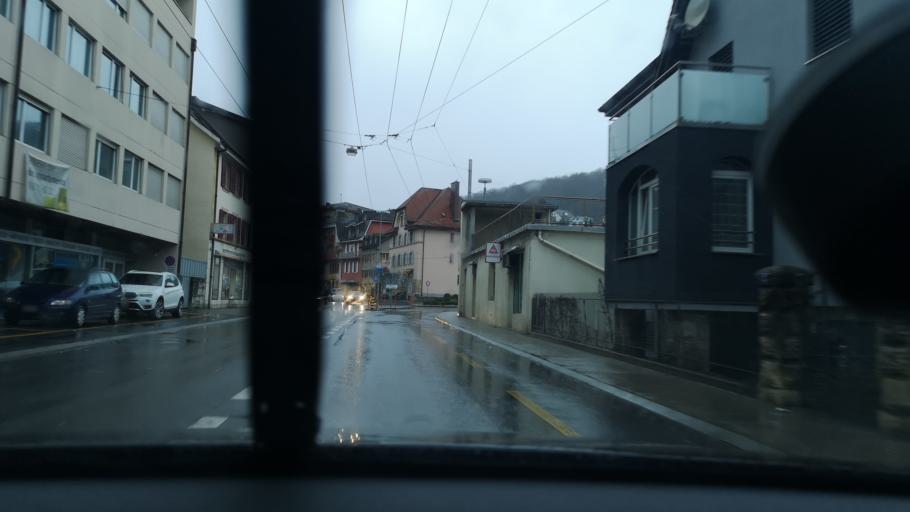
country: CH
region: Neuchatel
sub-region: Boudry District
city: Peseux
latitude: 46.9880
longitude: 6.8920
